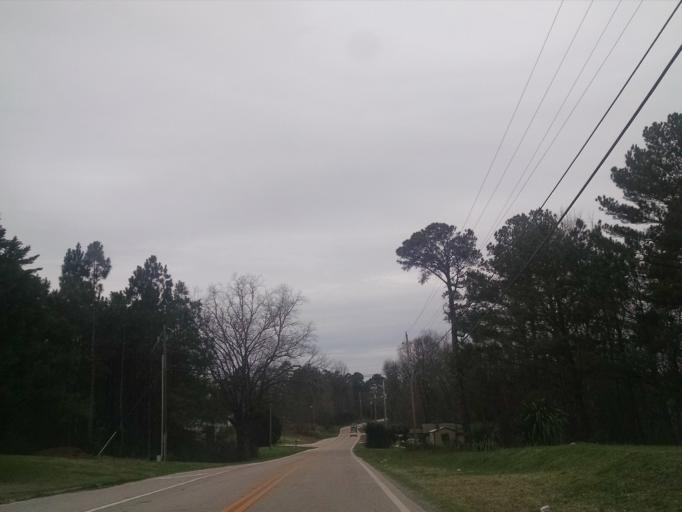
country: US
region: Georgia
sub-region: Hall County
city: Flowery Branch
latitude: 34.1766
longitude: -83.8938
